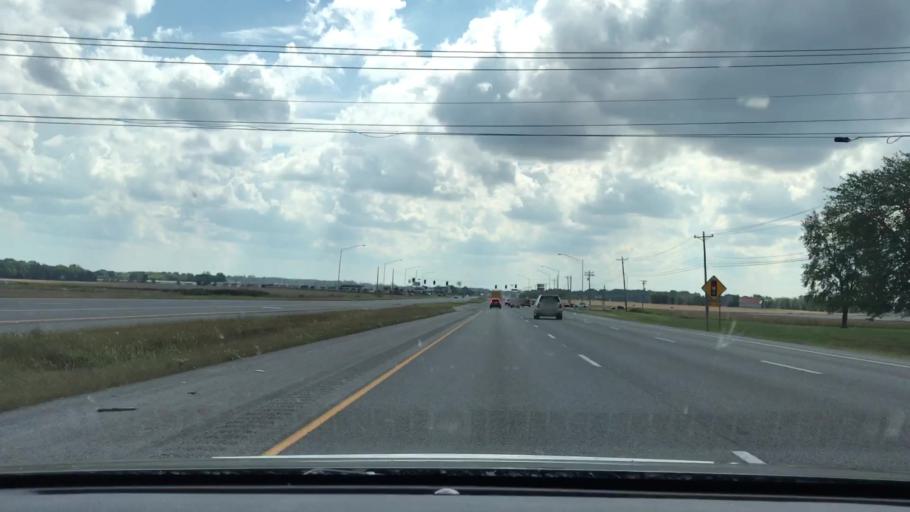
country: US
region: Kentucky
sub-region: Christian County
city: Oak Grove
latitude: 36.6784
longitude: -87.4470
